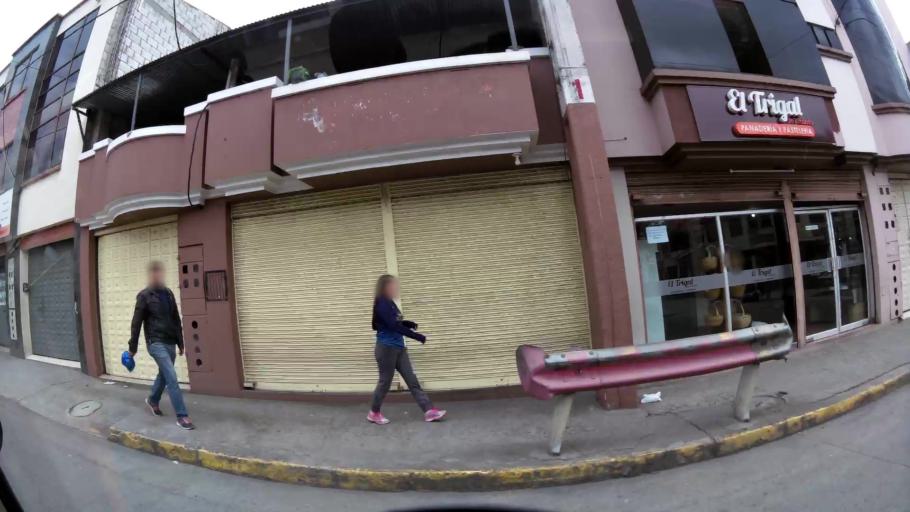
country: EC
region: Azuay
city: Cuenca
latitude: -2.9127
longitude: -79.0328
